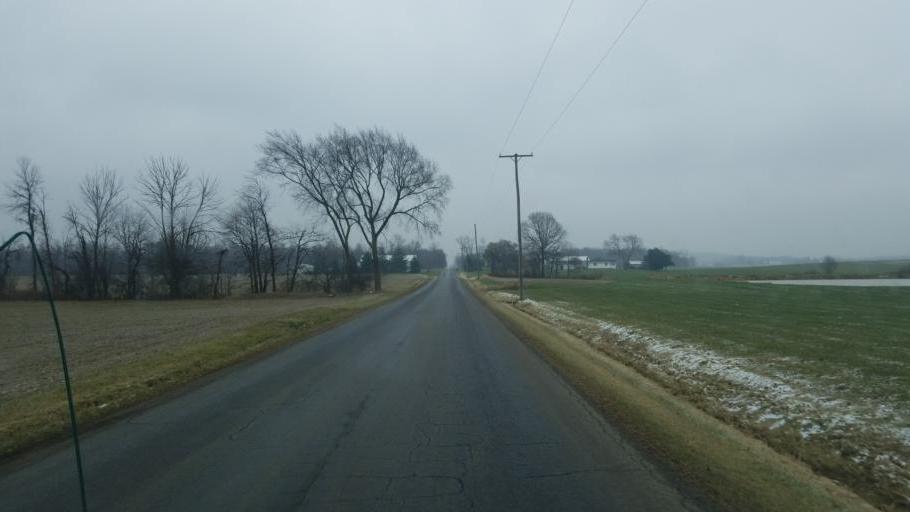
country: US
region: Ohio
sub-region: Huron County
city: Greenwich
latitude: 40.9755
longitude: -82.5148
